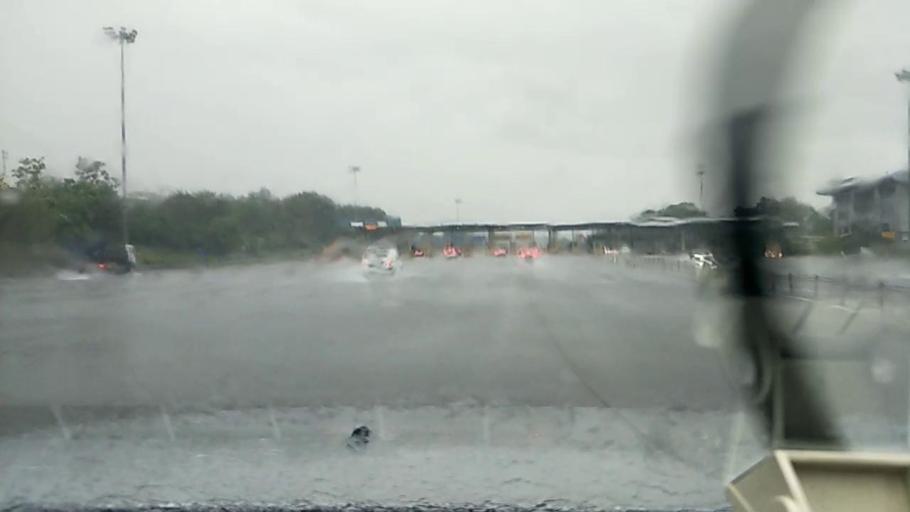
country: MY
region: Selangor
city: Kampong Baharu Balakong
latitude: 3.0062
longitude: 101.7709
